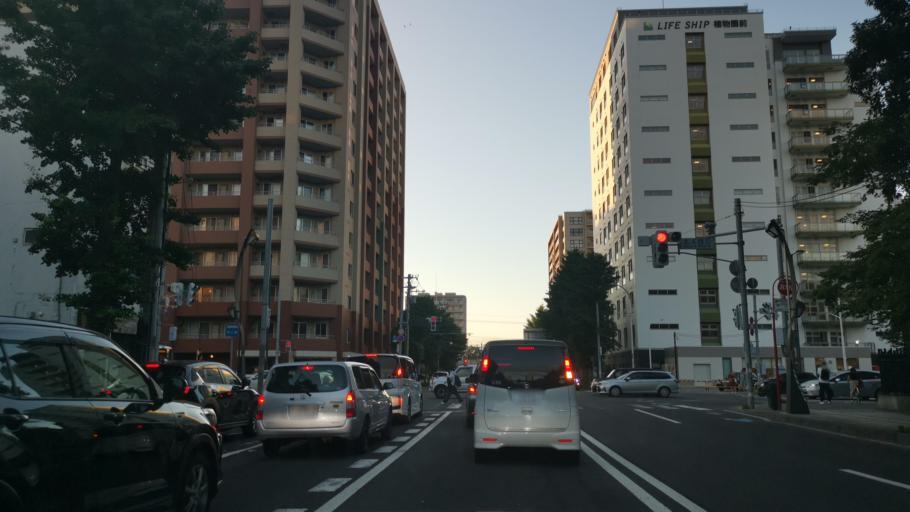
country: JP
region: Hokkaido
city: Sapporo
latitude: 43.0649
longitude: 141.3397
